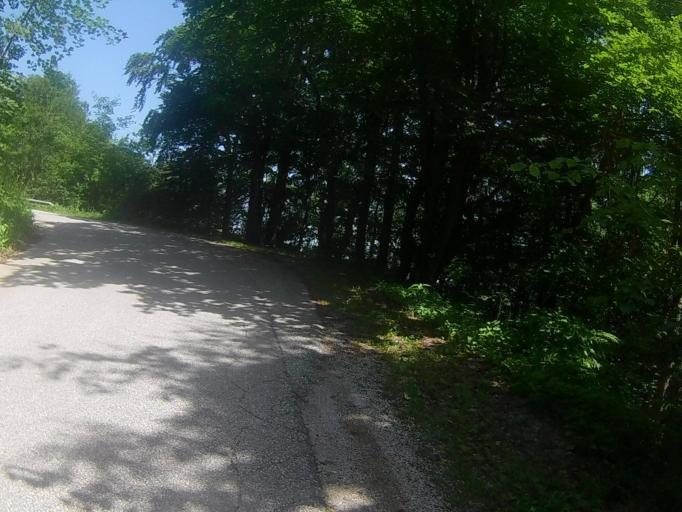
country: SI
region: Kungota
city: Zgornja Kungota
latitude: 46.6097
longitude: 15.5968
